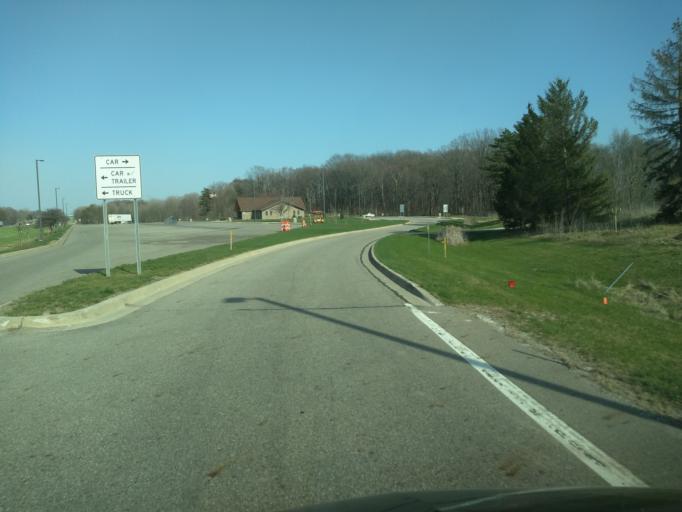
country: US
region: Michigan
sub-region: Clinton County
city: Wacousta
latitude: 42.7982
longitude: -84.7175
